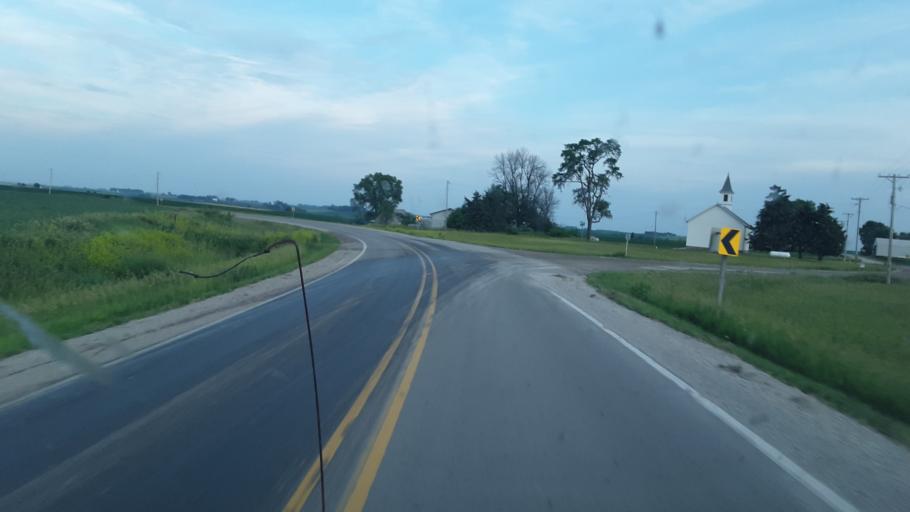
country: US
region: Iowa
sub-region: Iowa County
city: Marengo
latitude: 41.7048
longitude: -92.1826
